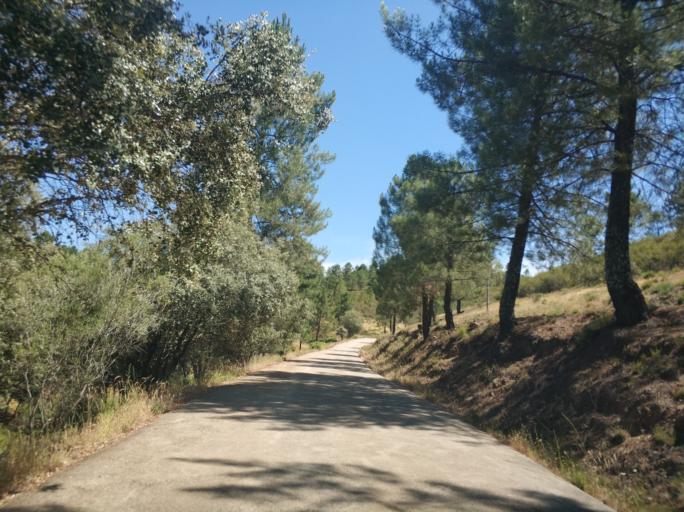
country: ES
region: Castille and Leon
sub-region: Provincia de Salamanca
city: Herguijuela de la Sierra
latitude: 40.4005
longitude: -6.0782
